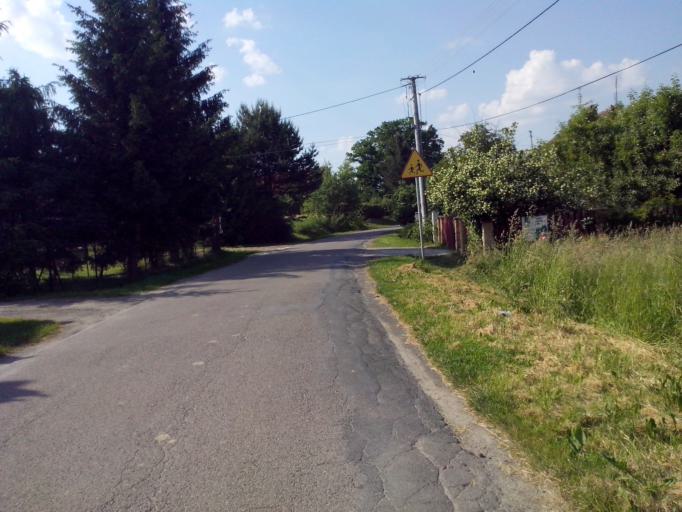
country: PL
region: Subcarpathian Voivodeship
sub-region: Powiat brzozowski
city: Blizne
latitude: 49.7385
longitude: 21.9769
